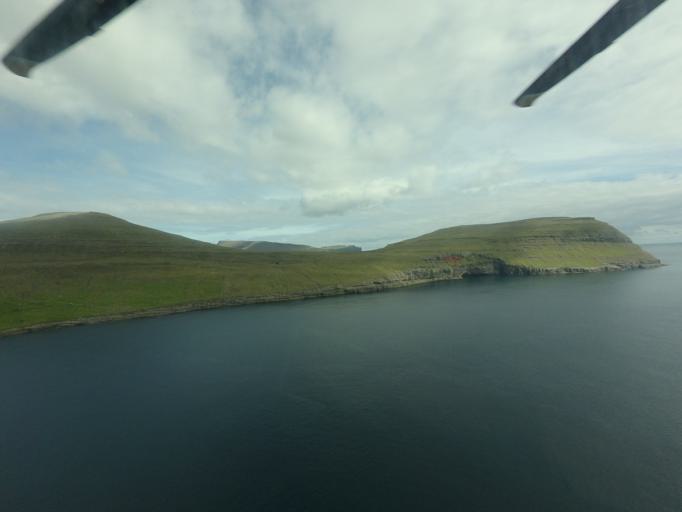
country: FO
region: Nordoyar
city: Klaksvik
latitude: 62.2738
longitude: -6.3271
